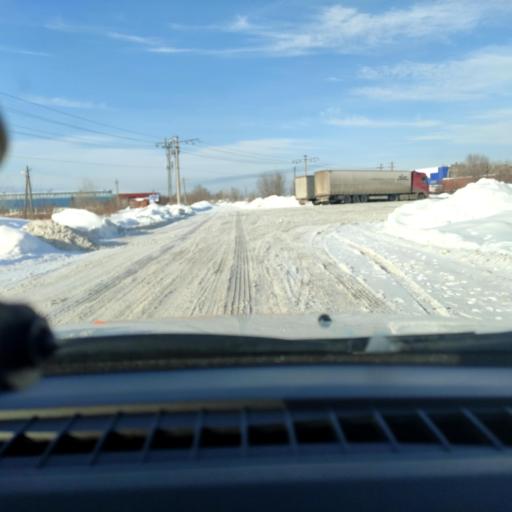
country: RU
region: Samara
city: Petra-Dubrava
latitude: 53.2622
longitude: 50.3538
